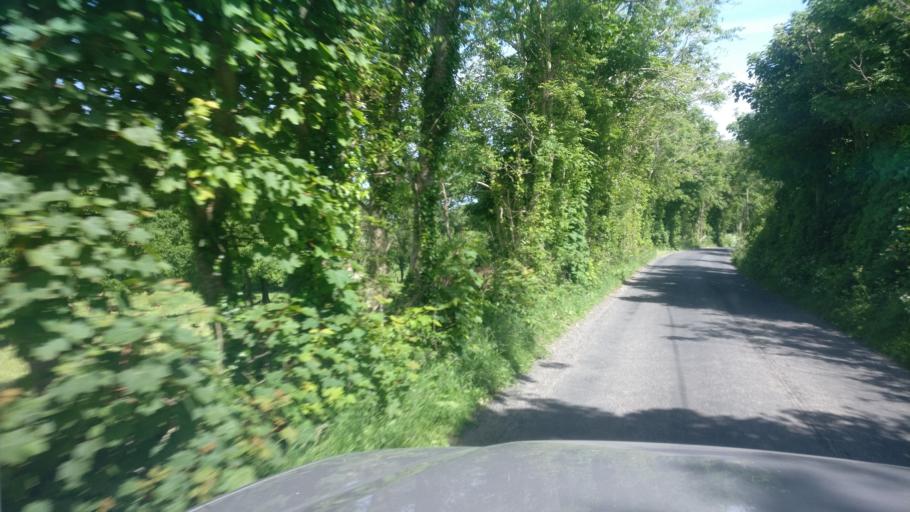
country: IE
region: Connaught
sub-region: County Galway
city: Gort
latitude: 53.1328
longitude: -8.7730
